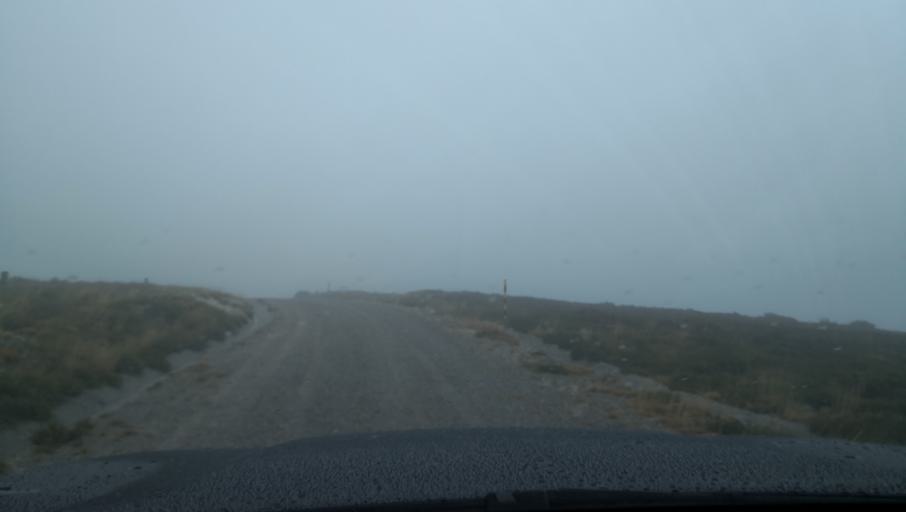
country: PT
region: Vila Real
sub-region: Vila Real
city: Vila Real
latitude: 41.3271
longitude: -7.8374
